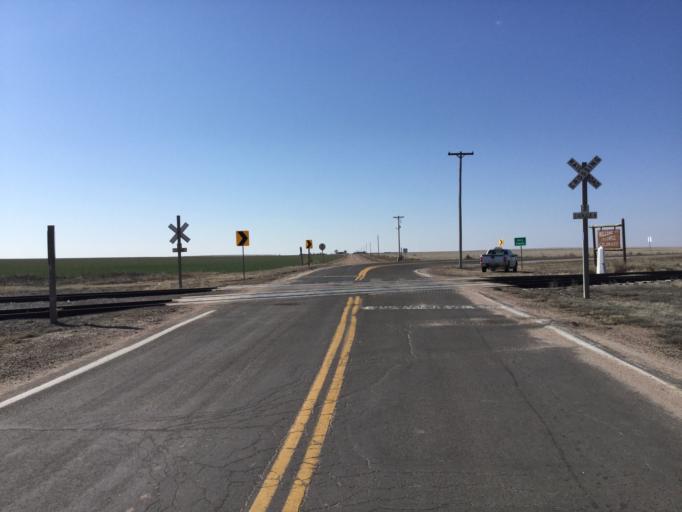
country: US
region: Kansas
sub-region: Stanton County
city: Johnson
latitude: 37.4699
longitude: -102.0418
